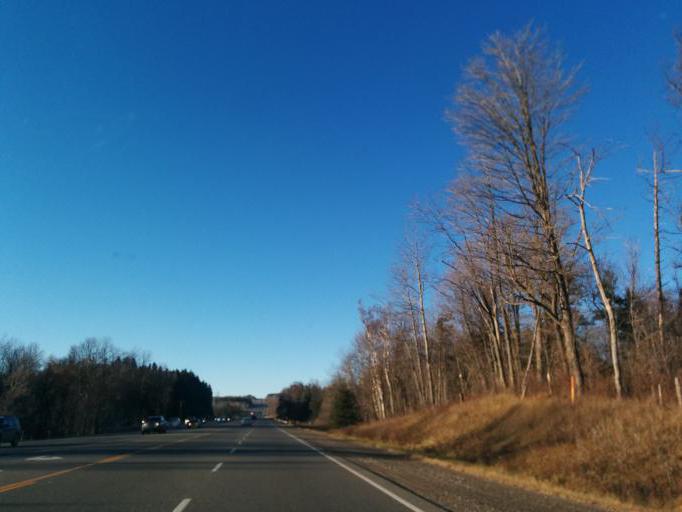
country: CA
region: Ontario
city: Orangeville
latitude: 43.8239
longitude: -79.9465
